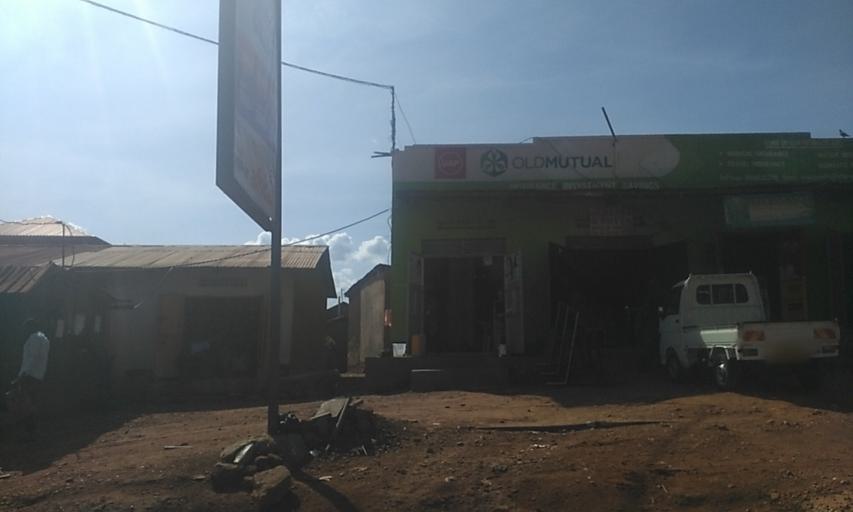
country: UG
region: Central Region
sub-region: Wakiso District
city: Kireka
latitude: 0.3787
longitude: 32.6257
